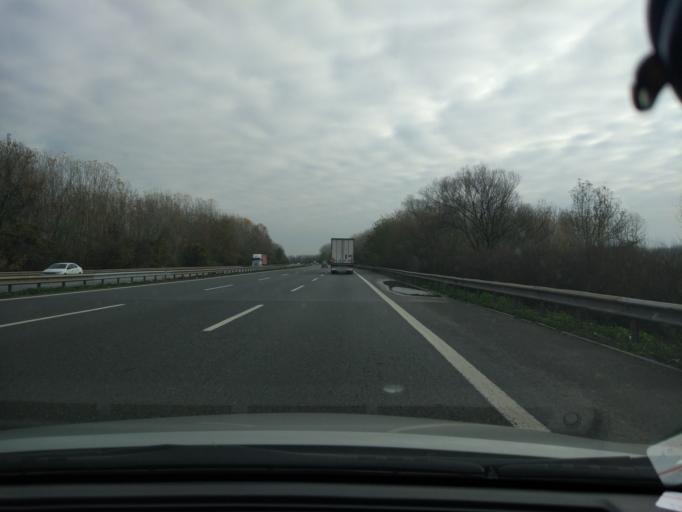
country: TR
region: Sakarya
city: Karapurcek
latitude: 40.7114
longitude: 30.5129
